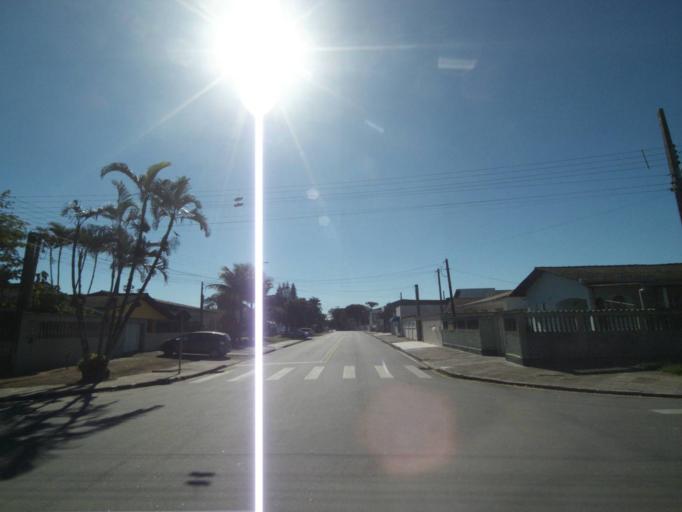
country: BR
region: Parana
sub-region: Paranagua
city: Paranagua
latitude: -25.5316
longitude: -48.5277
